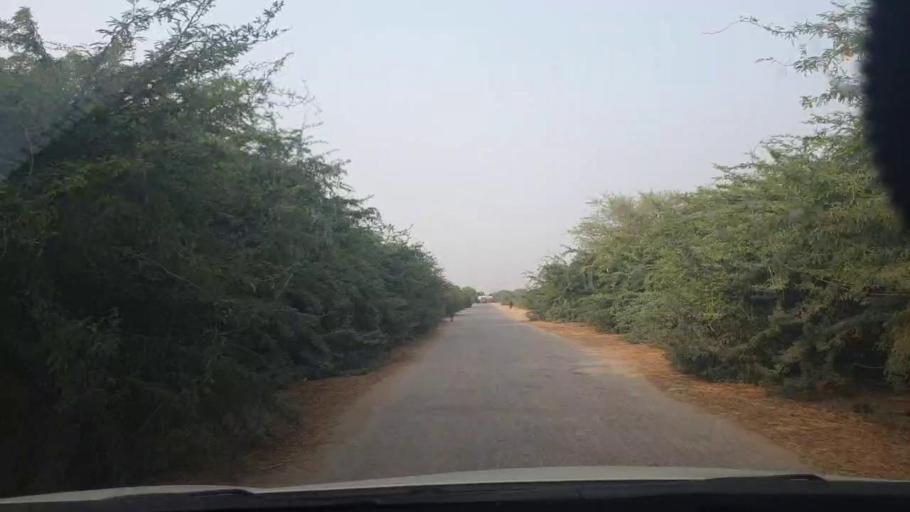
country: PK
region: Sindh
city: Bulri
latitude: 24.7654
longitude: 68.4204
